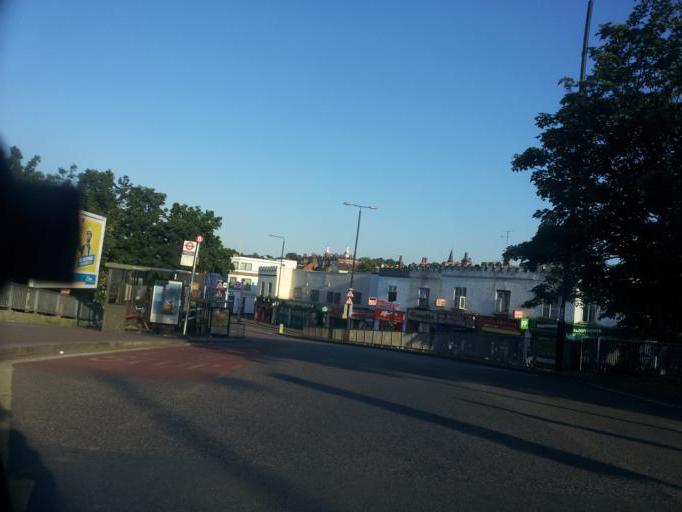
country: GB
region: England
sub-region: Greater London
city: Woolwich
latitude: 51.4898
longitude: 0.0854
